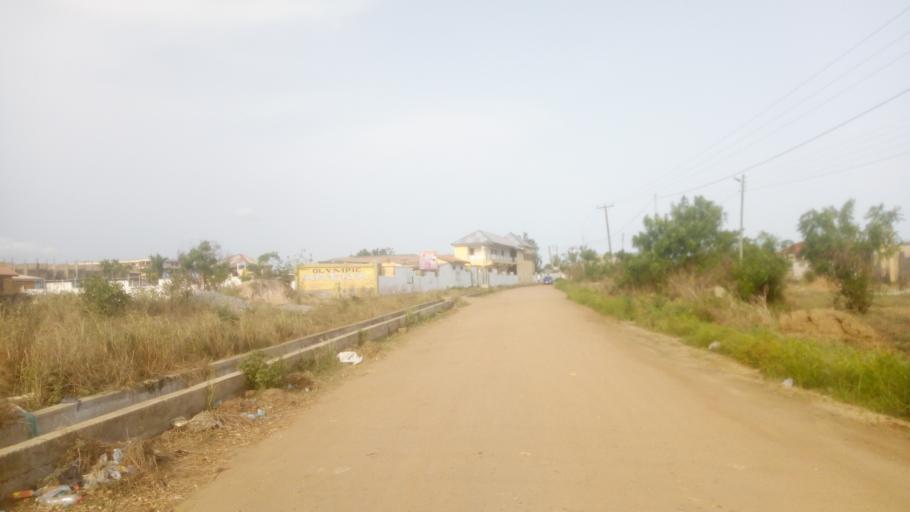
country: GH
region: Central
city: Winneba
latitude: 5.3771
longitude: -0.6353
